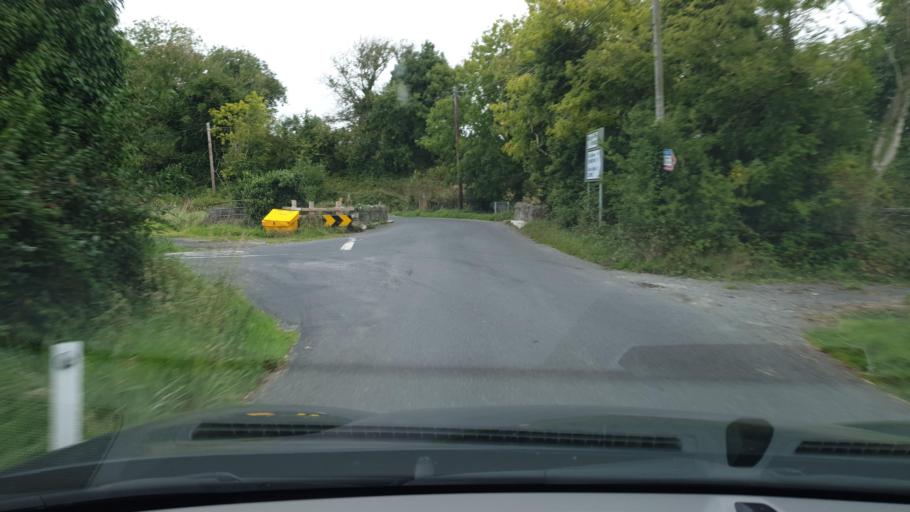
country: IE
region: Leinster
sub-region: An Mhi
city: Ratoath
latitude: 53.5104
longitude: -6.4857
